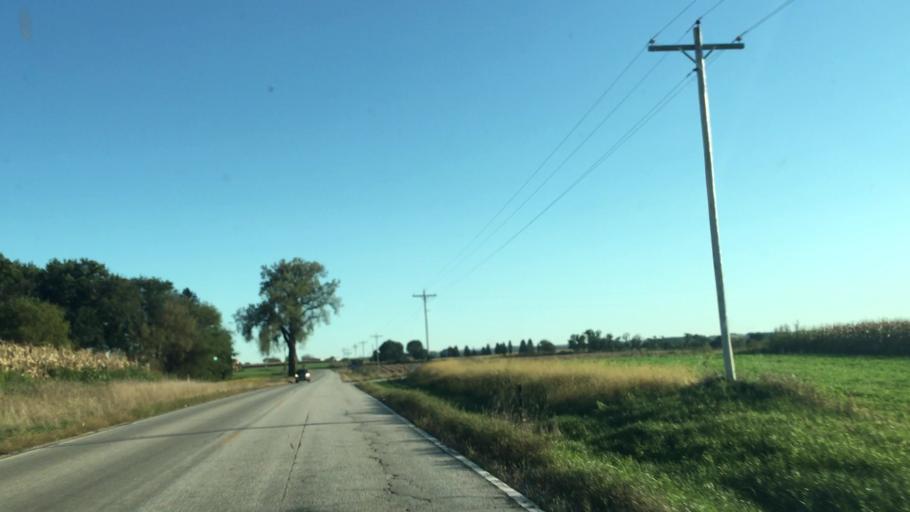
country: US
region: Minnesota
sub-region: Fillmore County
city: Chatfield
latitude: 43.8227
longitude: -92.0692
